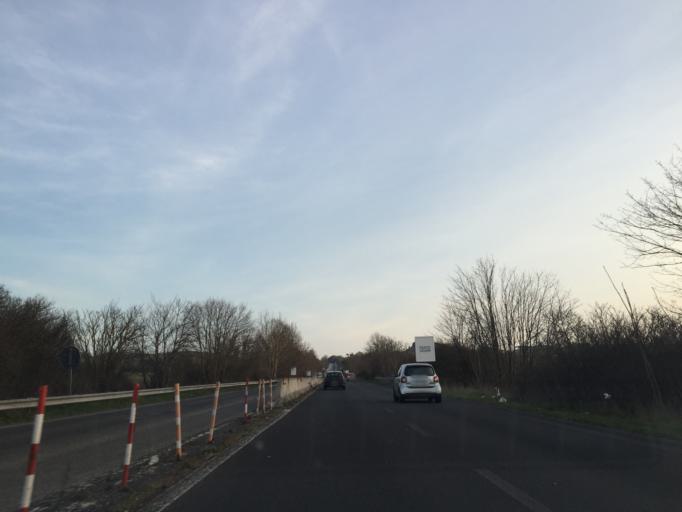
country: IT
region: Latium
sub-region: Citta metropolitana di Roma Capitale
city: Campagnano di Roma
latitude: 42.1486
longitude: 12.3495
